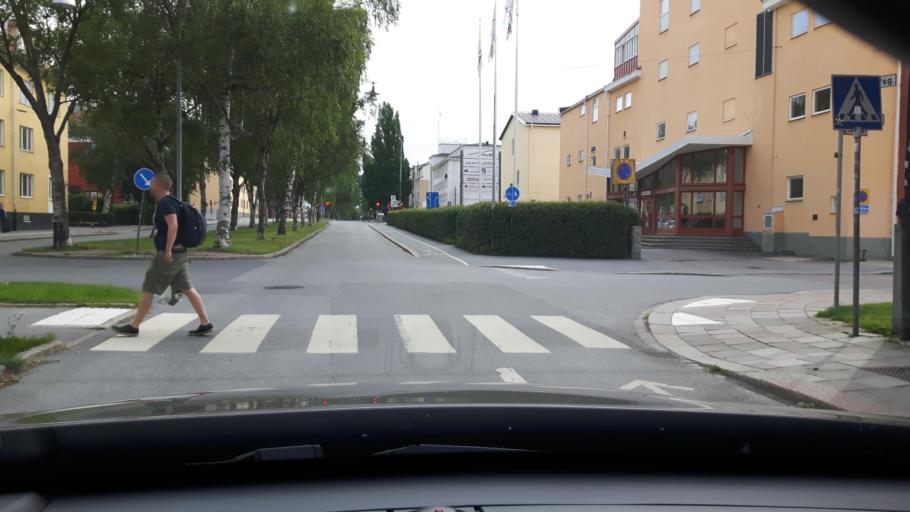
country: SE
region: Uppsala
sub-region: Uppsala Kommun
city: Uppsala
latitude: 59.8638
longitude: 17.6417
